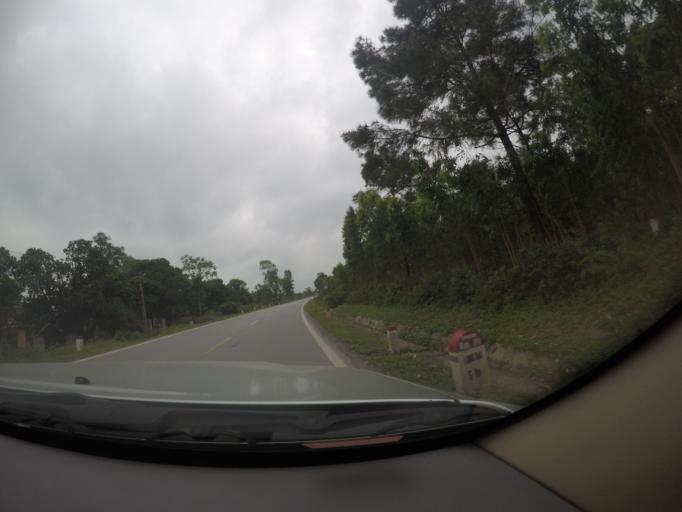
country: VN
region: Quang Binh
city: Quan Hau
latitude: 17.3674
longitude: 106.6221
